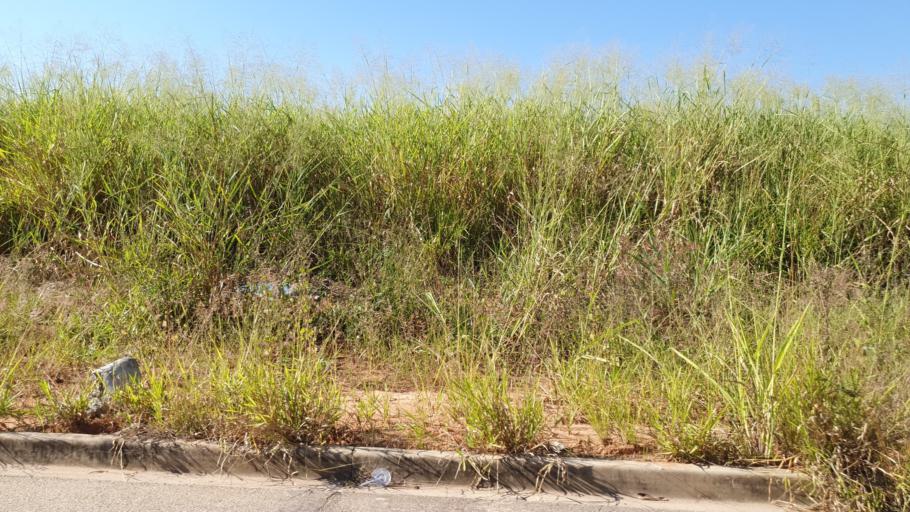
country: BR
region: Sao Paulo
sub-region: Sorocaba
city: Sorocaba
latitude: -23.4378
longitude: -47.4391
